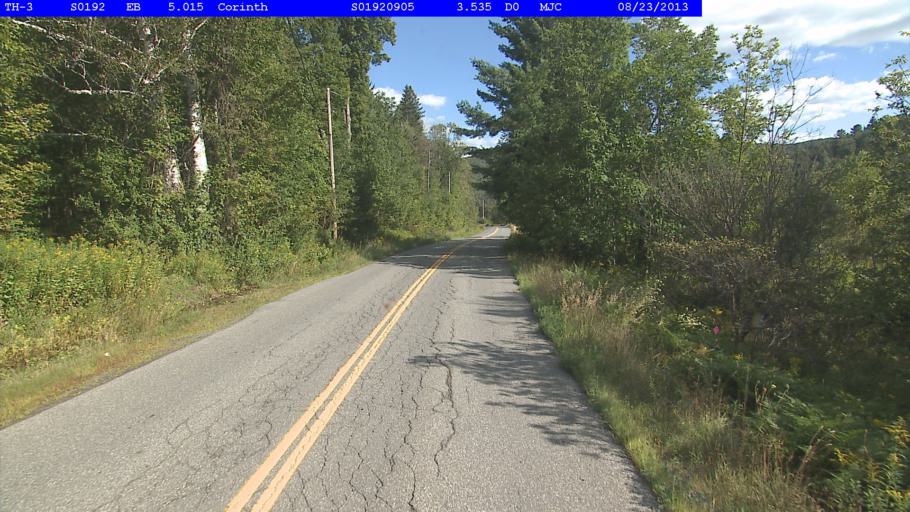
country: US
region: Vermont
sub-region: Orange County
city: Chelsea
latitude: 44.0026
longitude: -72.2921
